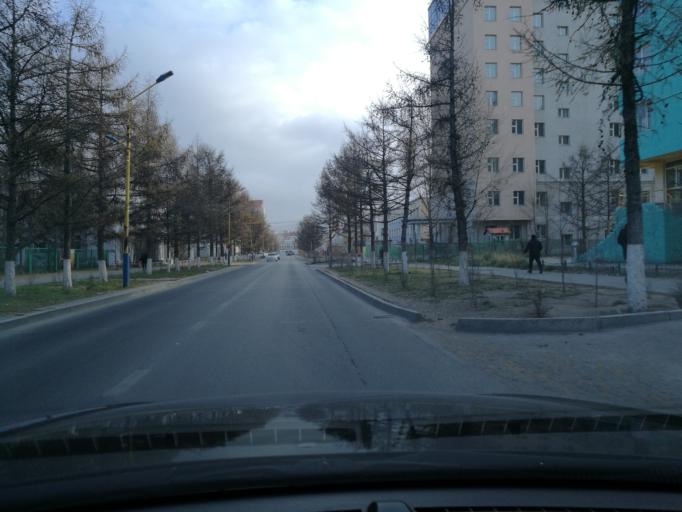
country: MN
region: Ulaanbaatar
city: Ulaanbaatar
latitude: 47.9257
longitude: 106.9272
